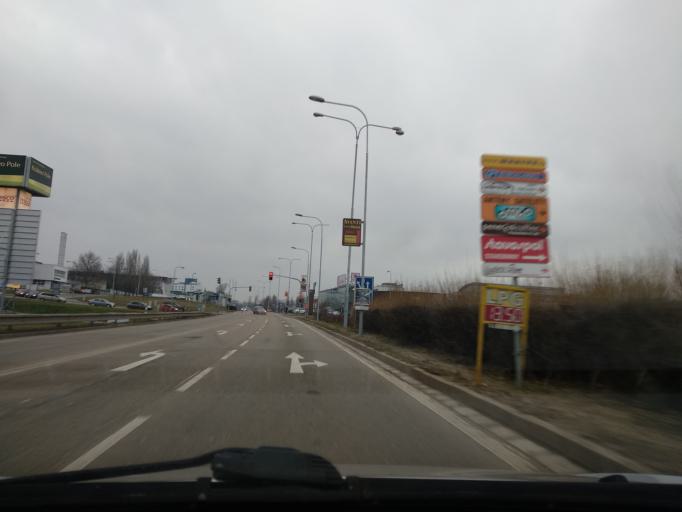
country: CZ
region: South Moravian
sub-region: Mesto Brno
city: Brno
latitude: 49.2174
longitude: 16.6039
